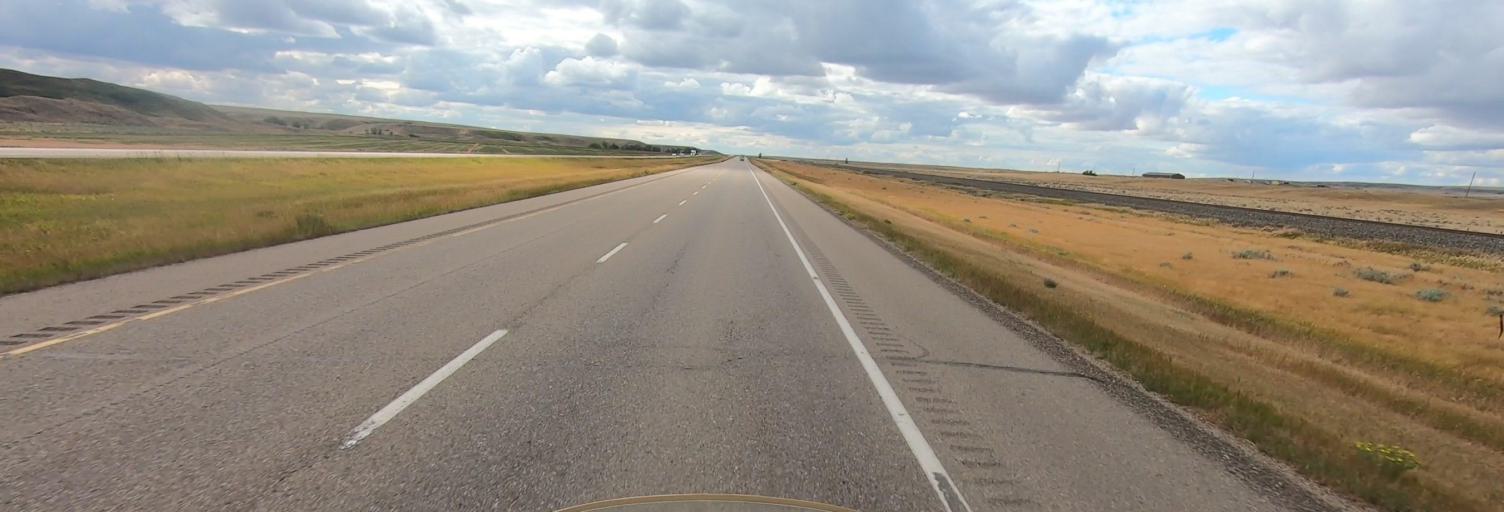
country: CA
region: Alberta
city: Medicine Hat
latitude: 49.9401
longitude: -110.1756
